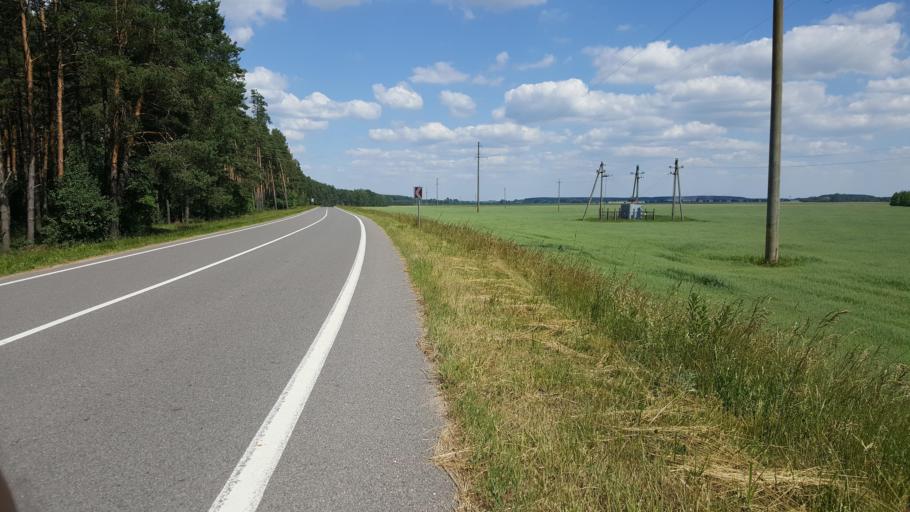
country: BY
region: Brest
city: Kamyanyuki
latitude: 52.5040
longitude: 23.6652
